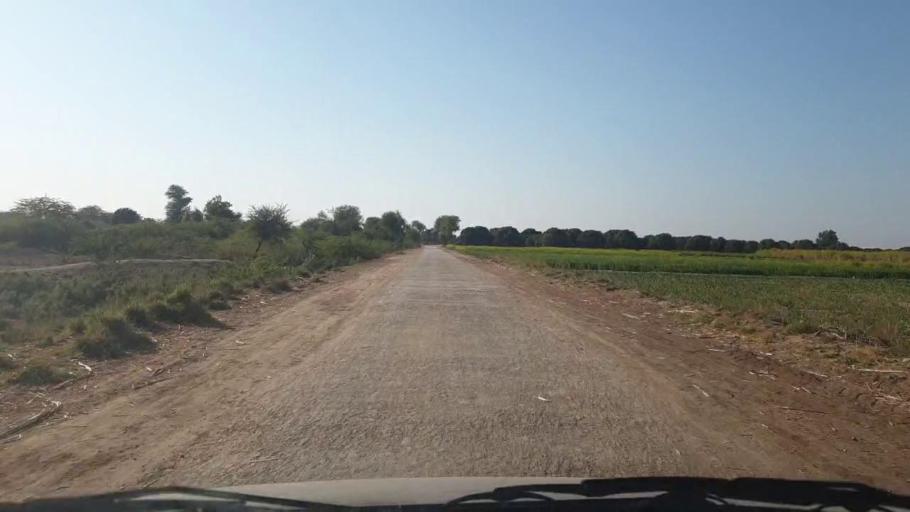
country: PK
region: Sindh
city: Samaro
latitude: 25.3516
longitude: 69.3116
